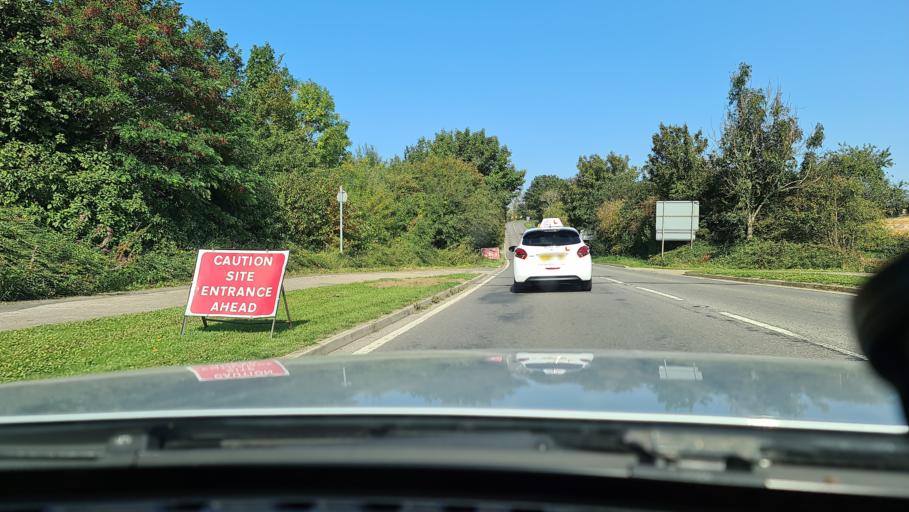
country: GB
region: England
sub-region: Northamptonshire
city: Daventry
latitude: 52.2821
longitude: -1.1685
